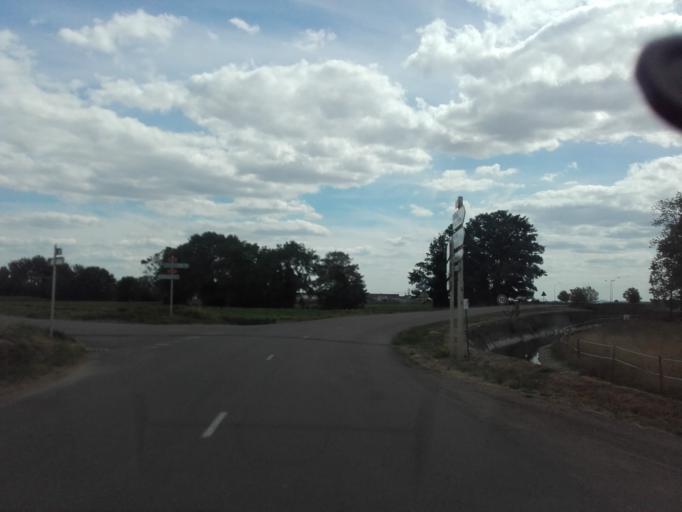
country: FR
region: Bourgogne
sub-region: Departement de la Cote-d'Or
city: Beaune
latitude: 47.0555
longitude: 4.8398
